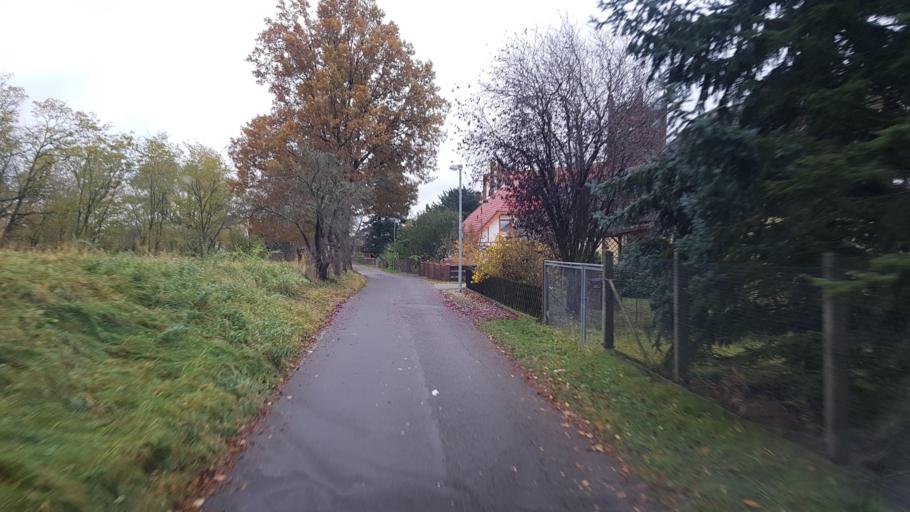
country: DE
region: Brandenburg
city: Drebkau
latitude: 51.6978
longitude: 14.2457
